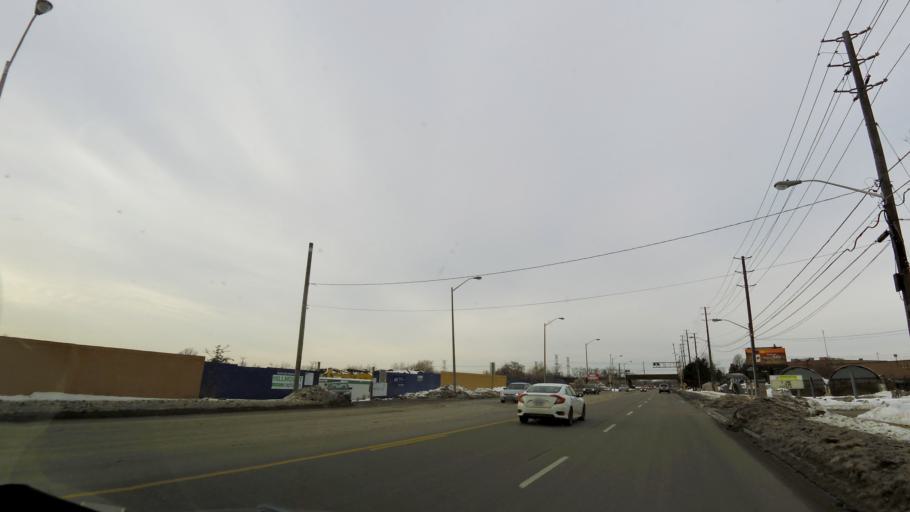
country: CA
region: Ontario
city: Concord
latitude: 43.7662
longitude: -79.5760
